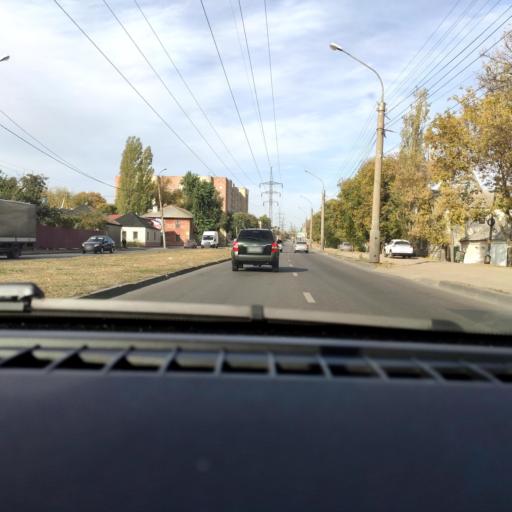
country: RU
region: Voronezj
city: Voronezh
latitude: 51.6385
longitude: 39.1646
